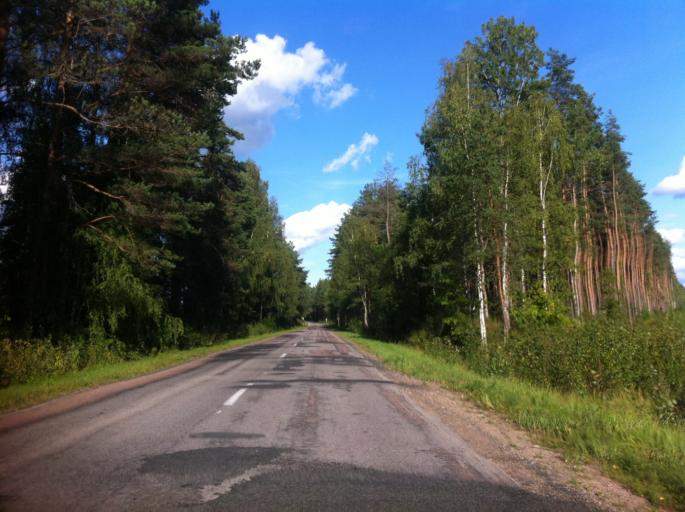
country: RU
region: Pskov
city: Izborsk
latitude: 57.8034
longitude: 27.7928
